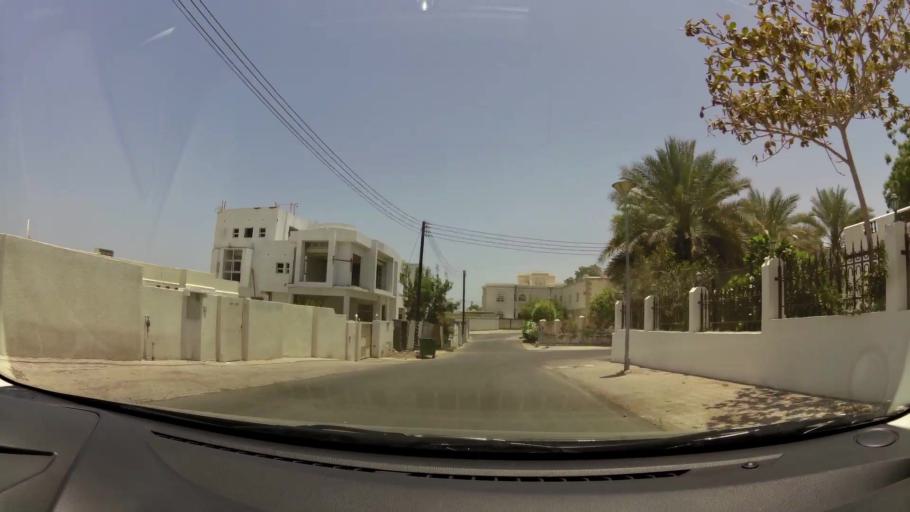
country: OM
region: Muhafazat Masqat
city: Bawshar
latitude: 23.6049
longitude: 58.4565
